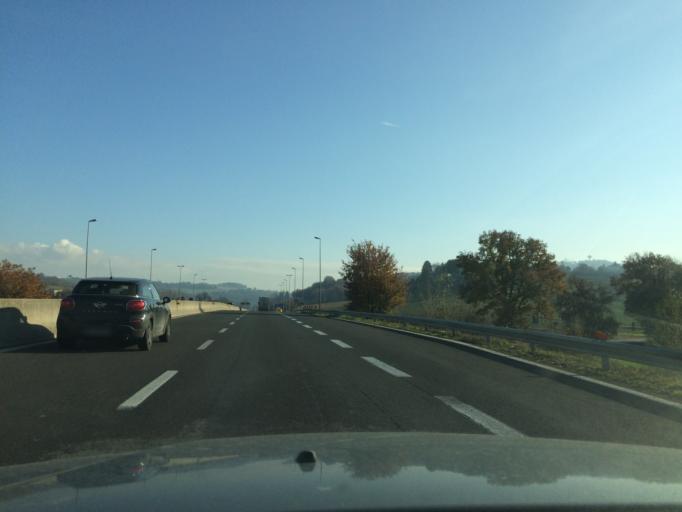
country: IT
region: Umbria
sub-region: Provincia di Perugia
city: Todi
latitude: 42.7876
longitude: 12.4281
